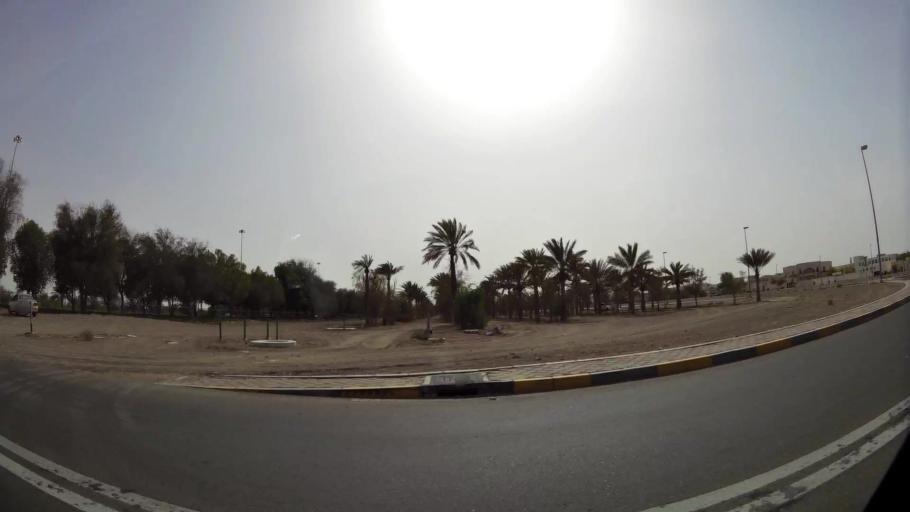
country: AE
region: Abu Dhabi
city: Al Ain
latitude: 24.2028
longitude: 55.5781
